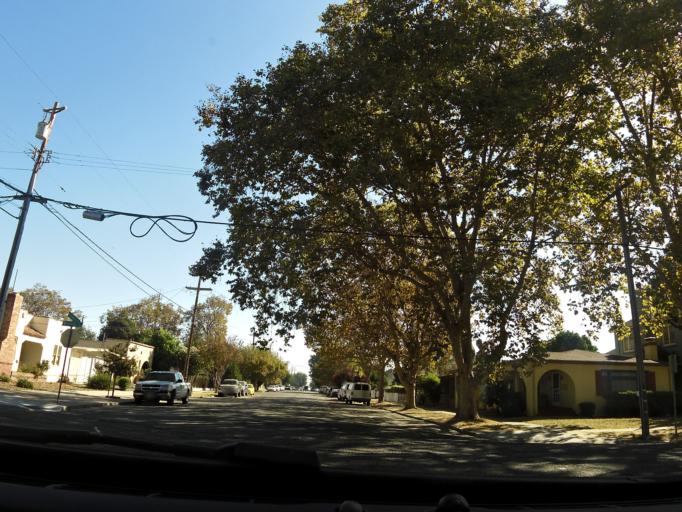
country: US
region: California
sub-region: San Benito County
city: Hollister
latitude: 36.8464
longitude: -121.4041
